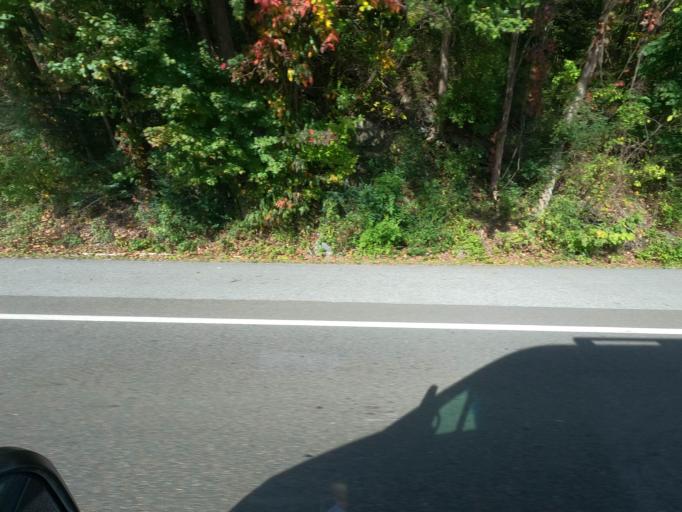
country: US
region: Tennessee
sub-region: Sullivan County
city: Walnut Hill
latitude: 36.5896
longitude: -82.2705
